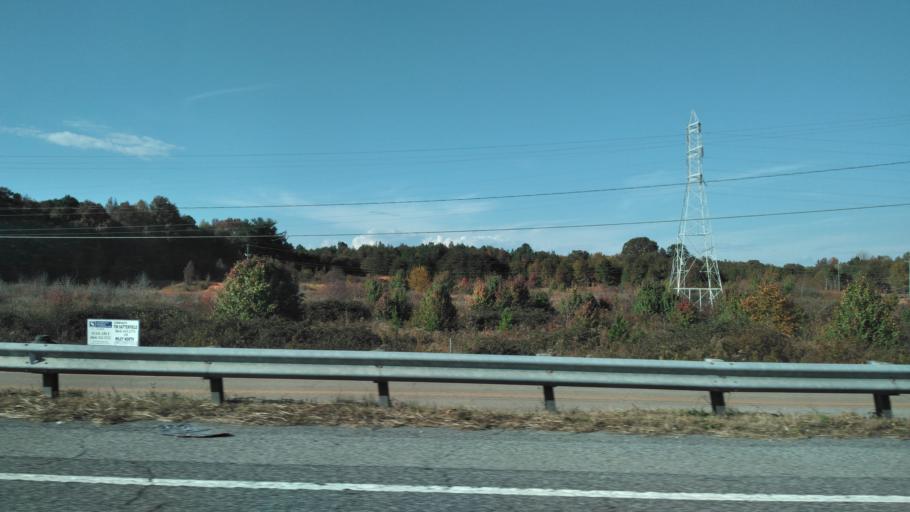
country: US
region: South Carolina
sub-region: Spartanburg County
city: Fairforest
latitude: 34.9671
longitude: -82.0105
